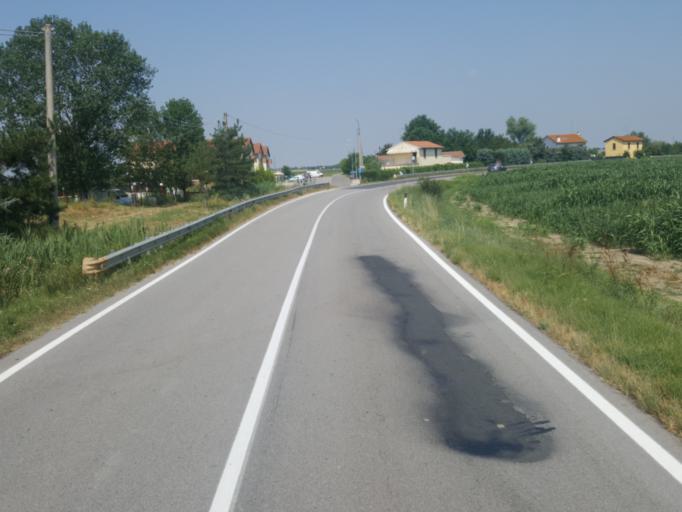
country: IT
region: Emilia-Romagna
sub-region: Provincia di Ravenna
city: Massa Lombarda
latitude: 44.4576
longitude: 11.7916
